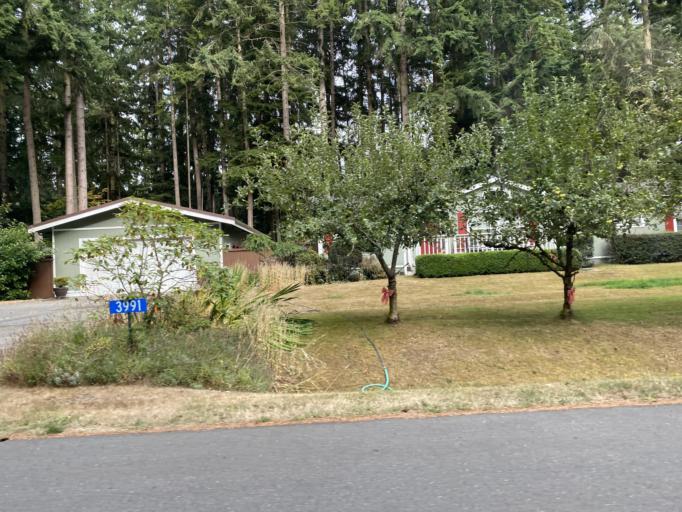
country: US
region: Washington
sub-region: Island County
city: Freeland
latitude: 48.0664
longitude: -122.5115
